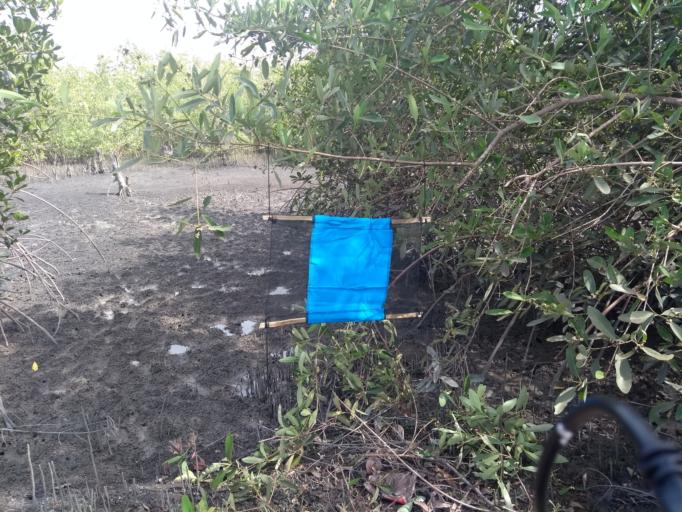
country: GN
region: Kindia
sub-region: Prefecture de Dubreka
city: Dubreka
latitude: 9.7719
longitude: -13.5296
